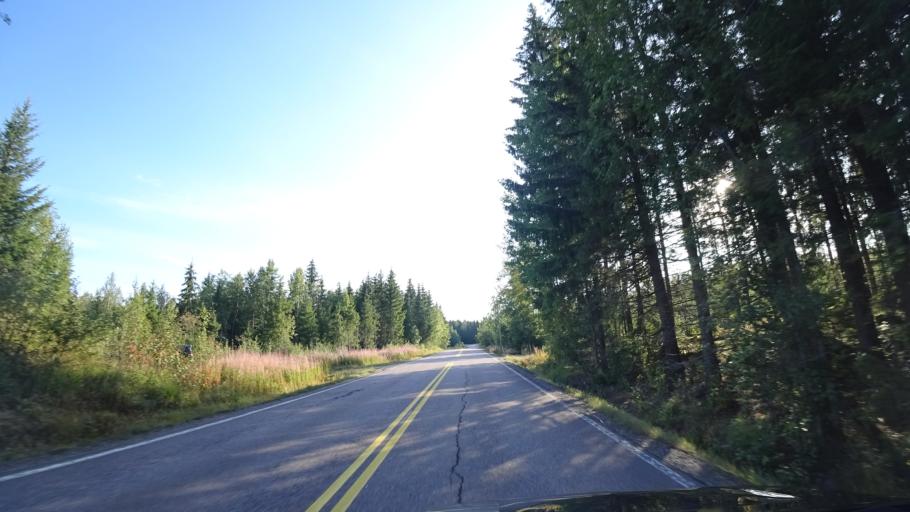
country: FI
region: Paijanne Tavastia
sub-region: Lahti
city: Hollola
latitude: 61.1630
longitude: 25.3614
